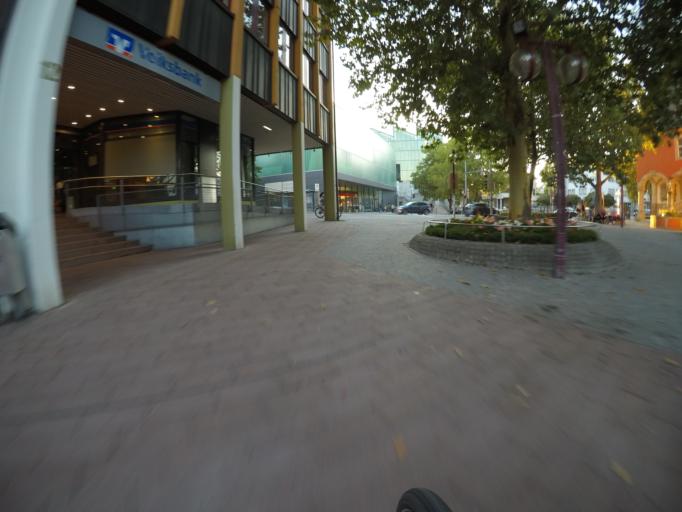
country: DE
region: Baden-Wuerttemberg
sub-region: Regierungsbezirk Stuttgart
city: Steinenbronn
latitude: 48.7310
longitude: 9.1098
